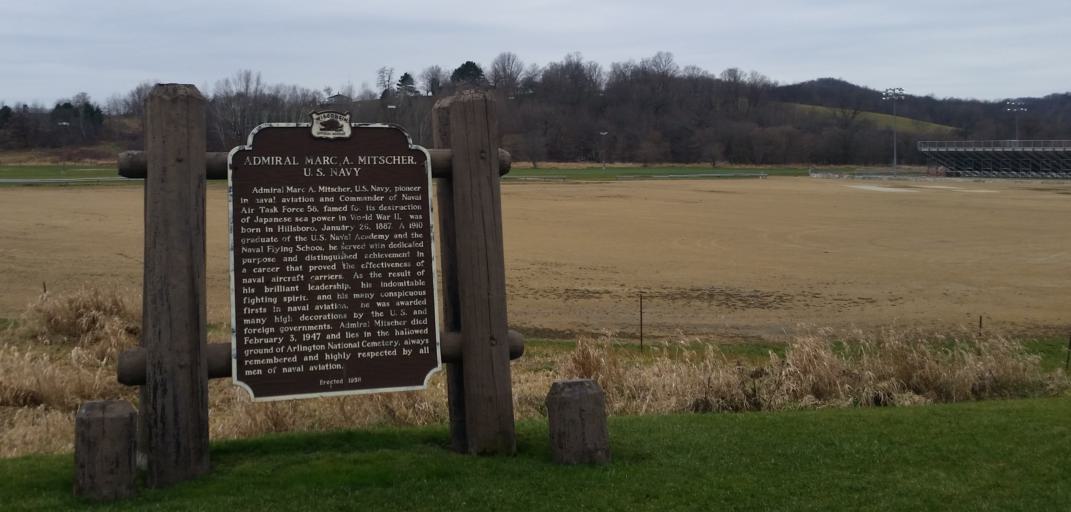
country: US
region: Wisconsin
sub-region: Vernon County
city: Hillsboro
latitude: 43.6522
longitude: -90.3440
